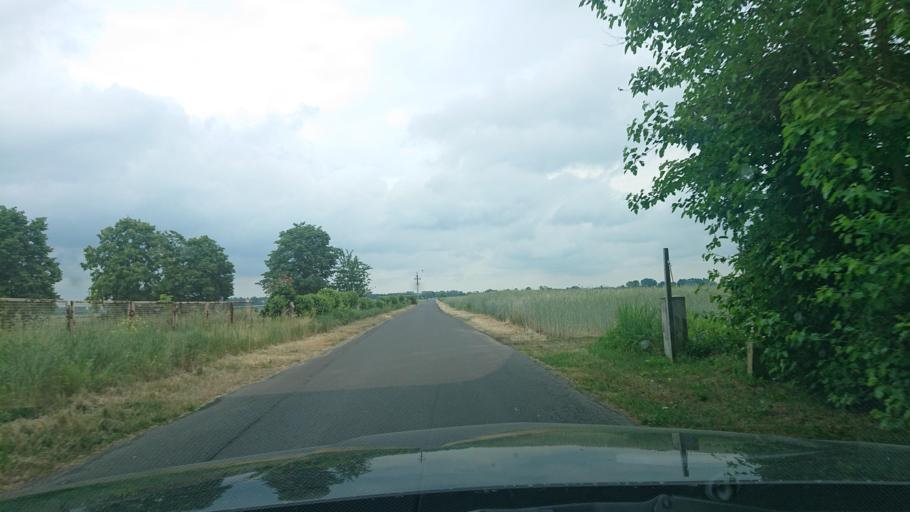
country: PL
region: Greater Poland Voivodeship
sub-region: Powiat gnieznienski
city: Czerniejewo
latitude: 52.4791
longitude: 17.5174
